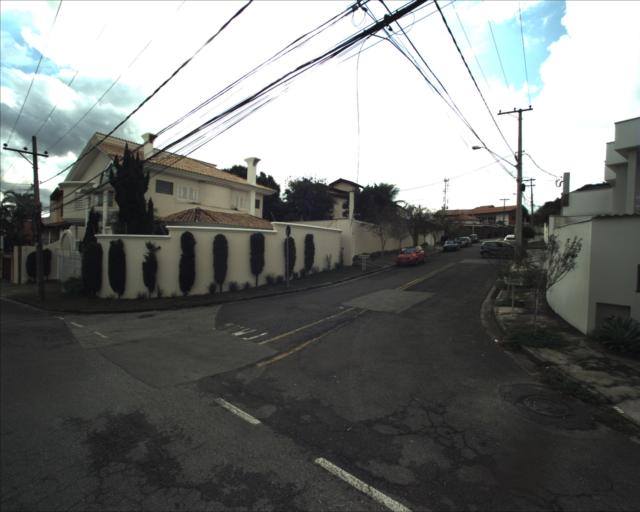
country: BR
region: Sao Paulo
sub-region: Sorocaba
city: Sorocaba
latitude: -23.5233
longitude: -47.4746
